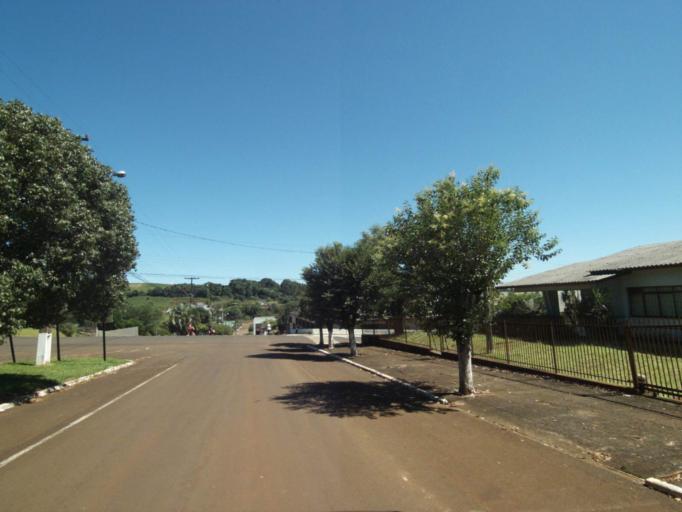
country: BR
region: Santa Catarina
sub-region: Sao Lourenco Do Oeste
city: Sao Lourenco dOeste
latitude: -26.2679
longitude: -52.7820
